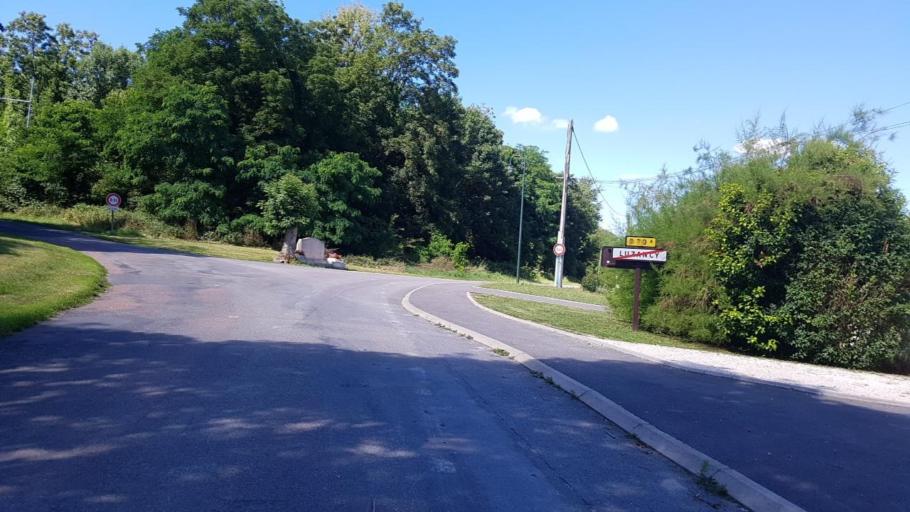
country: FR
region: Ile-de-France
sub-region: Departement de Seine-et-Marne
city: Chamigny
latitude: 48.9728
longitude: 3.1801
